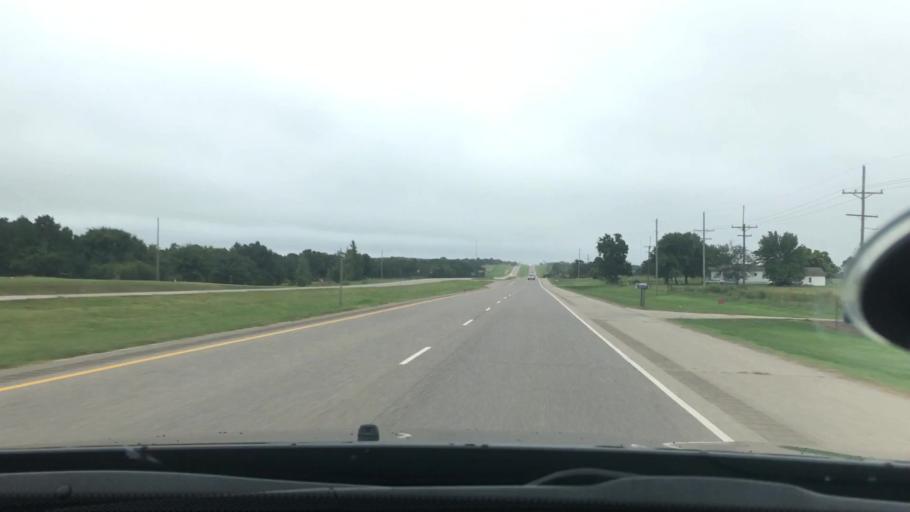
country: US
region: Oklahoma
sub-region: Seminole County
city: Seminole
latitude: 35.3523
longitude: -96.6715
